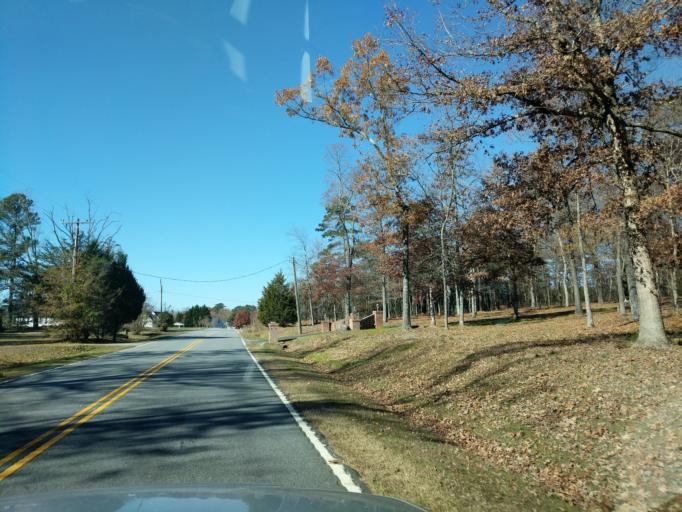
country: US
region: South Carolina
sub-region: Spartanburg County
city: Landrum
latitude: 35.0763
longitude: -82.2005
